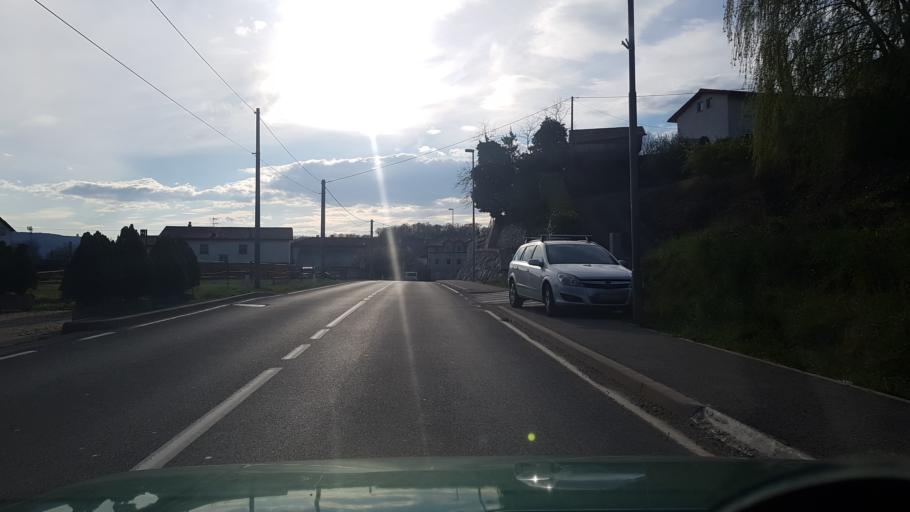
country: SI
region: Rence-Vogrsko
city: Volcja Draga
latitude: 45.9044
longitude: 13.6793
